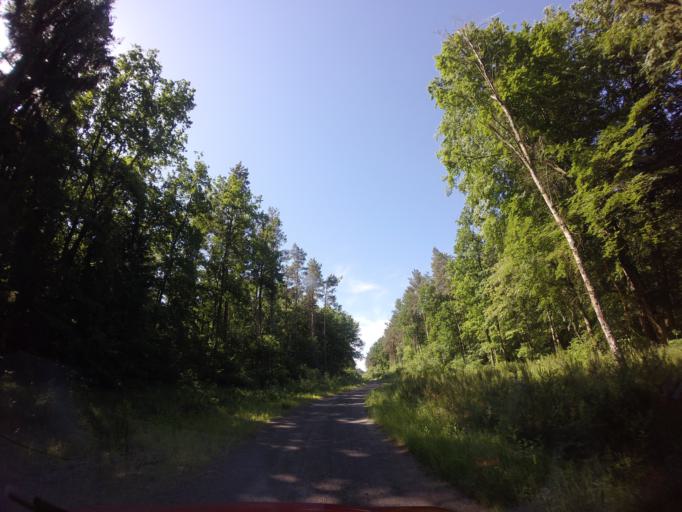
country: PL
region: West Pomeranian Voivodeship
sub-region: Powiat choszczenski
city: Choszczno
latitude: 53.1903
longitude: 15.3636
